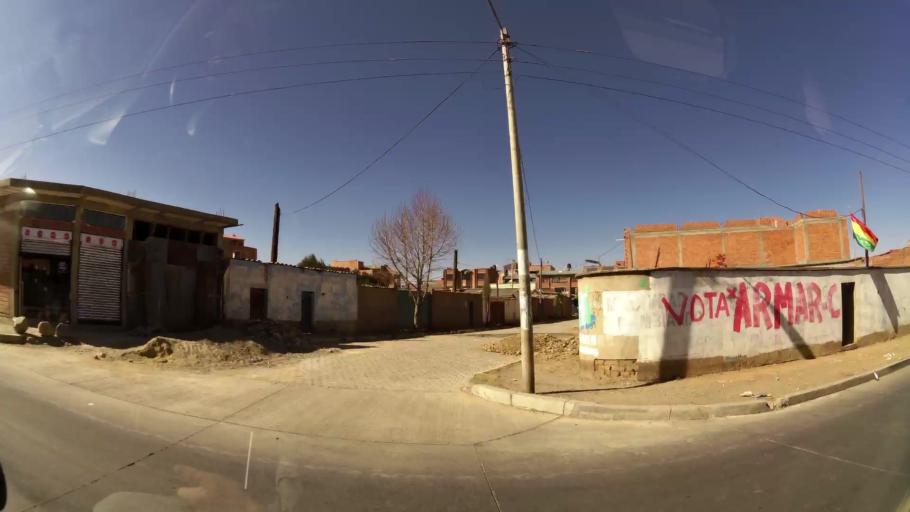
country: BO
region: La Paz
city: La Paz
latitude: -16.5165
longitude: -68.1806
